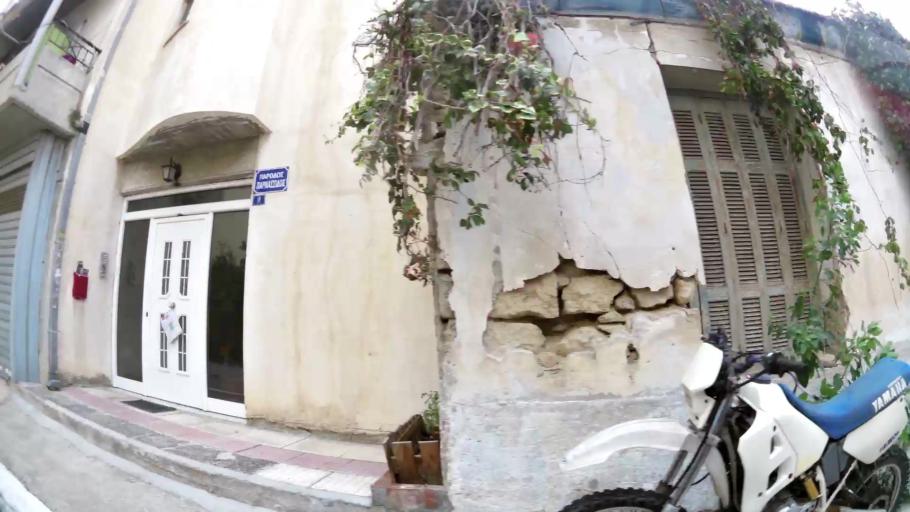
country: GR
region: Attica
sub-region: Nomos Piraios
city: Agios Ioannis Rentis
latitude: 37.9506
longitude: 23.6590
